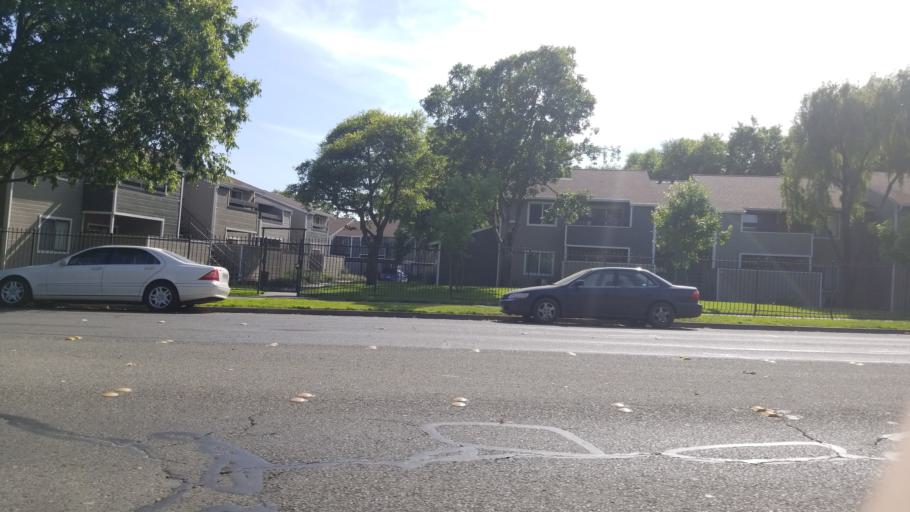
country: US
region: California
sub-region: Sonoma County
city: Roseland
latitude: 38.4358
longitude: -122.7280
